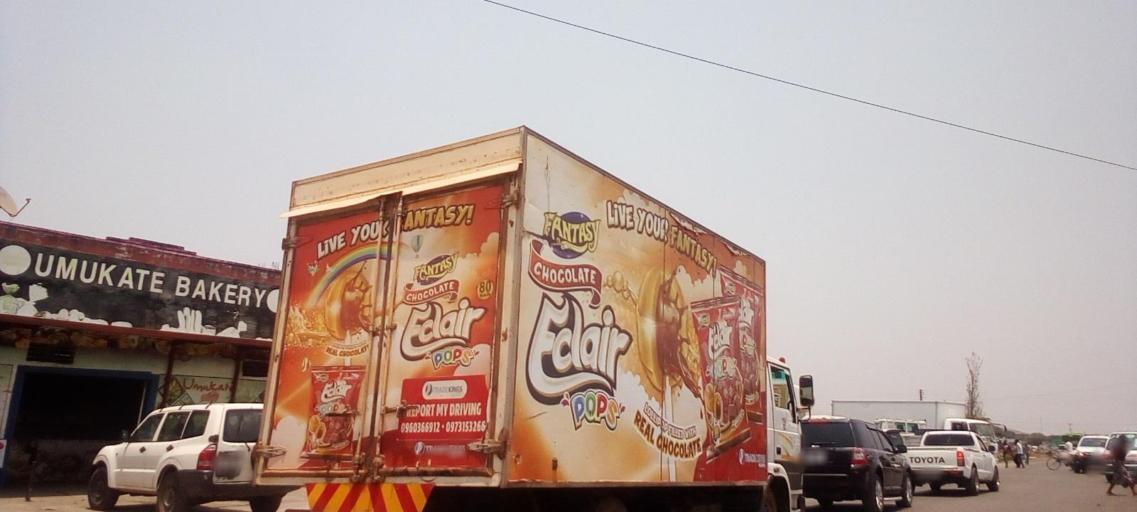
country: ZM
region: Lusaka
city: Lusaka
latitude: -15.4440
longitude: 28.2487
